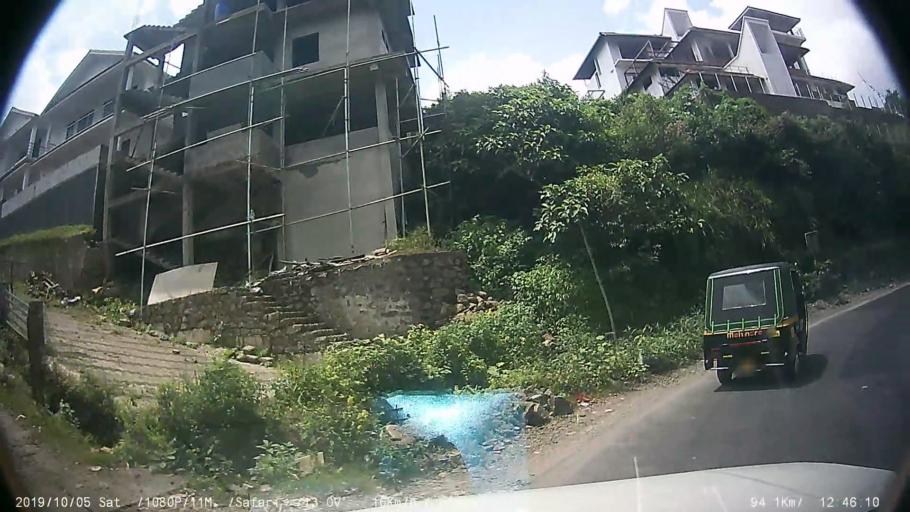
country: IN
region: Kerala
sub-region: Kottayam
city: Erattupetta
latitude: 9.5804
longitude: 76.9727
